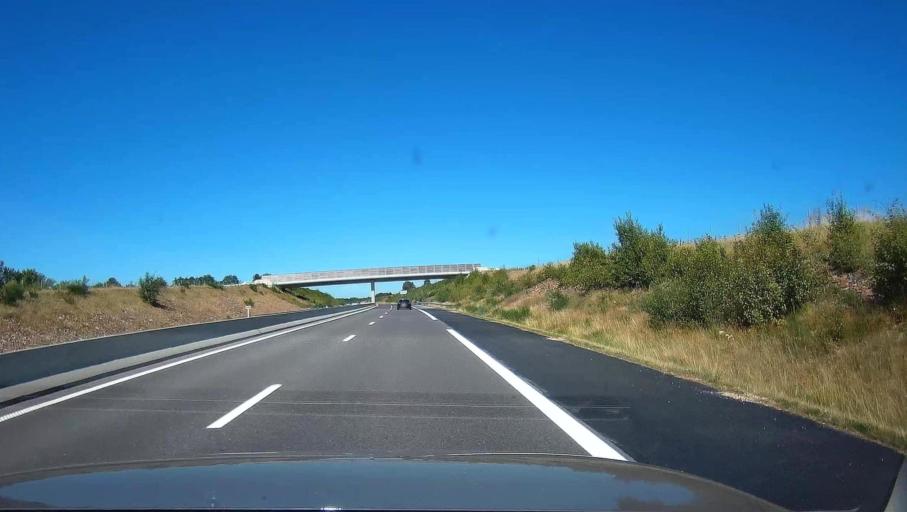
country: FR
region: Champagne-Ardenne
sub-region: Departement des Ardennes
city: Rocroi
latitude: 49.8866
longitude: 4.5183
